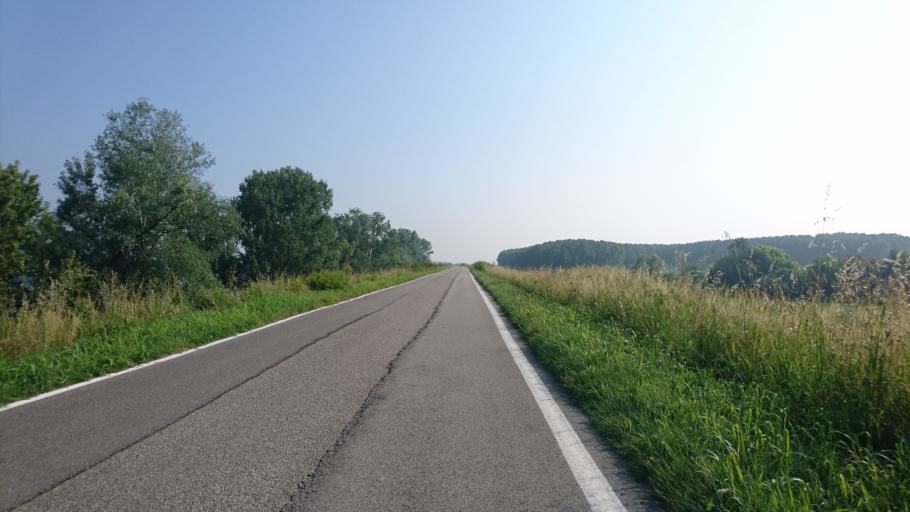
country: IT
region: Veneto
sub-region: Provincia di Rovigo
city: Castelnovo Bariano
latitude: 45.0374
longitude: 11.2683
